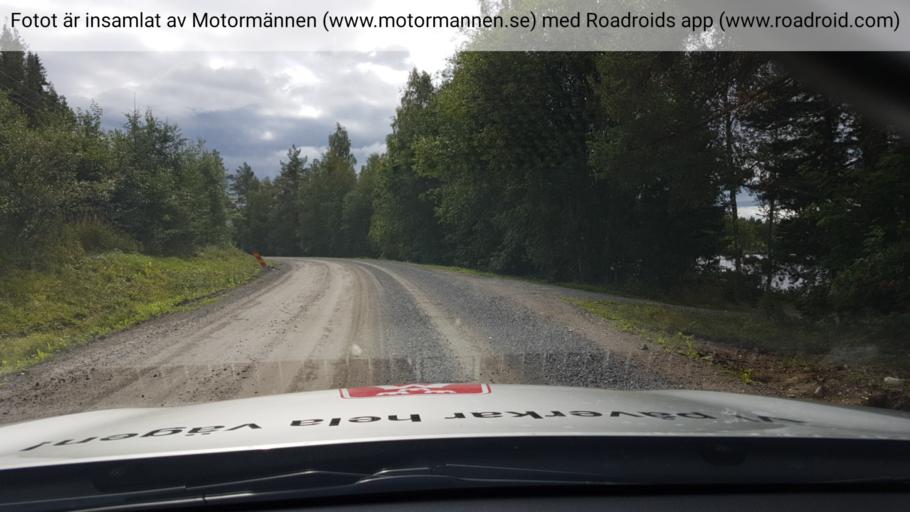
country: SE
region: Jaemtland
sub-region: Ragunda Kommun
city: Hammarstrand
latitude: 62.9550
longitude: 16.1158
